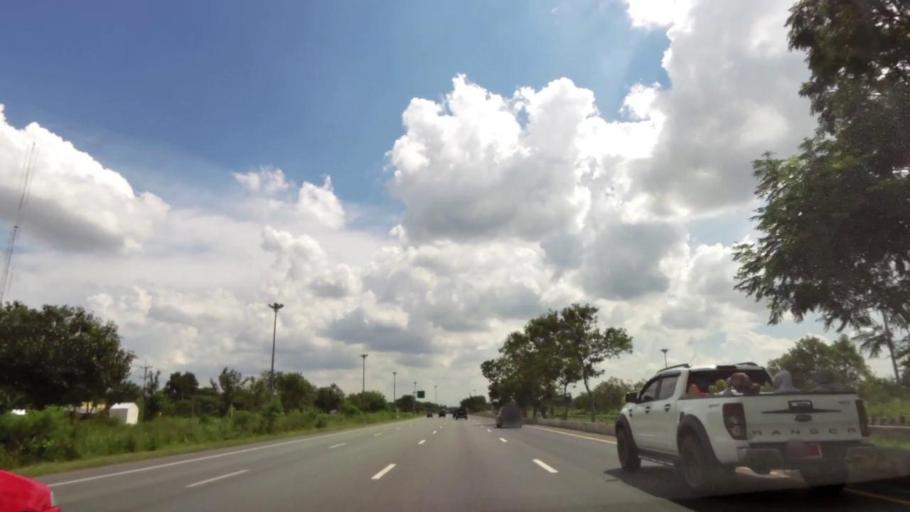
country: TH
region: Phra Nakhon Si Ayutthaya
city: Bang Pahan
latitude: 14.4495
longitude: 100.5409
